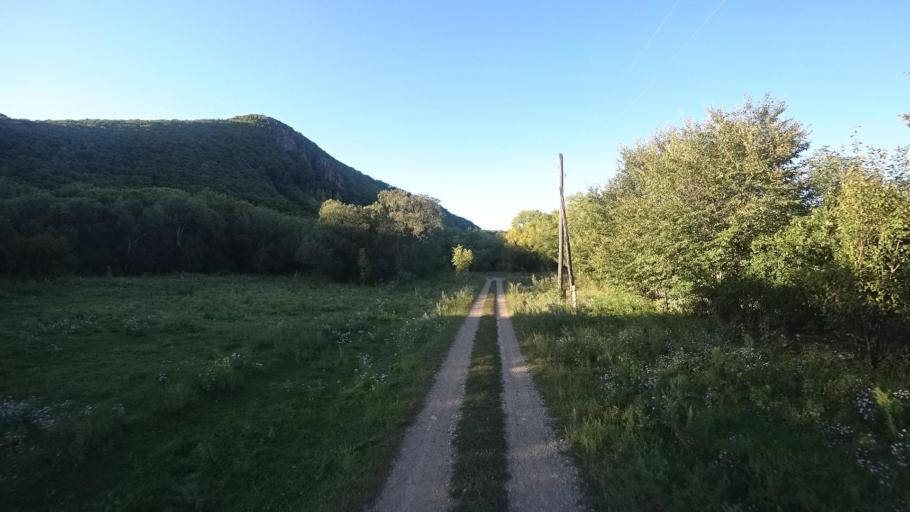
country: RU
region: Primorskiy
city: Kirovskiy
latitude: 44.8343
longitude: 133.5732
